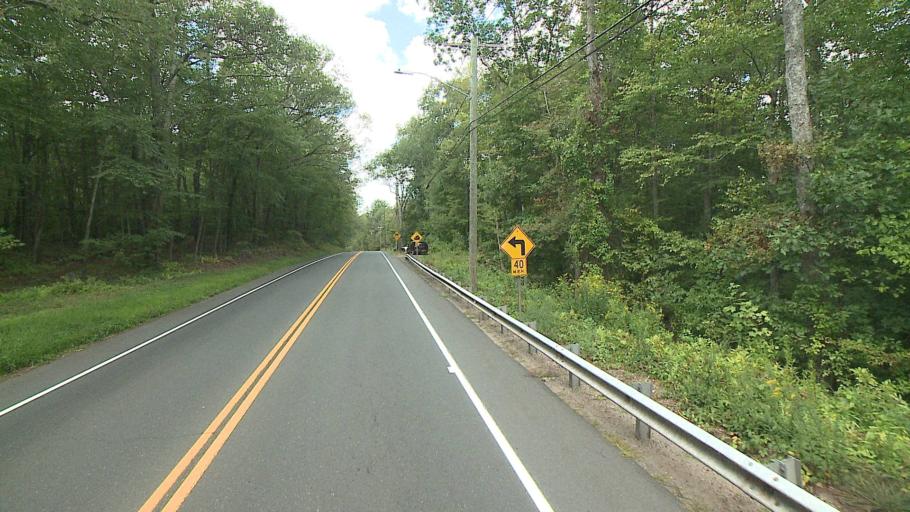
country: US
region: Connecticut
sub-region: Tolland County
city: Coventry Lake
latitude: 41.7989
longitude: -72.3413
